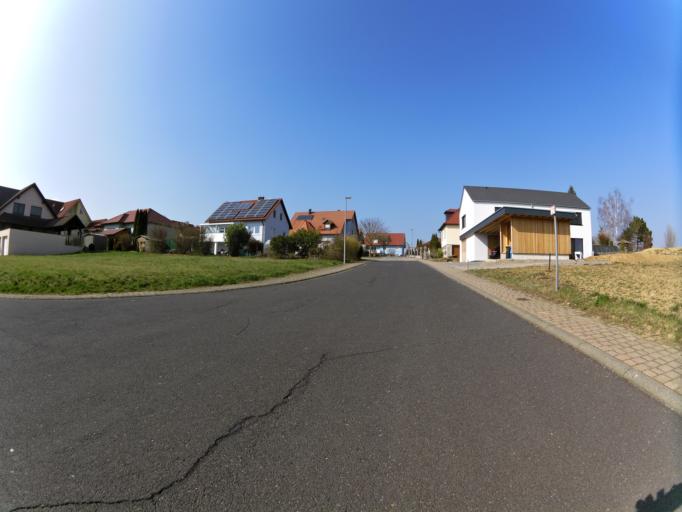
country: DE
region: Bavaria
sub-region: Regierungsbezirk Unterfranken
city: Sulzdorf
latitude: 49.6531
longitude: 9.9070
